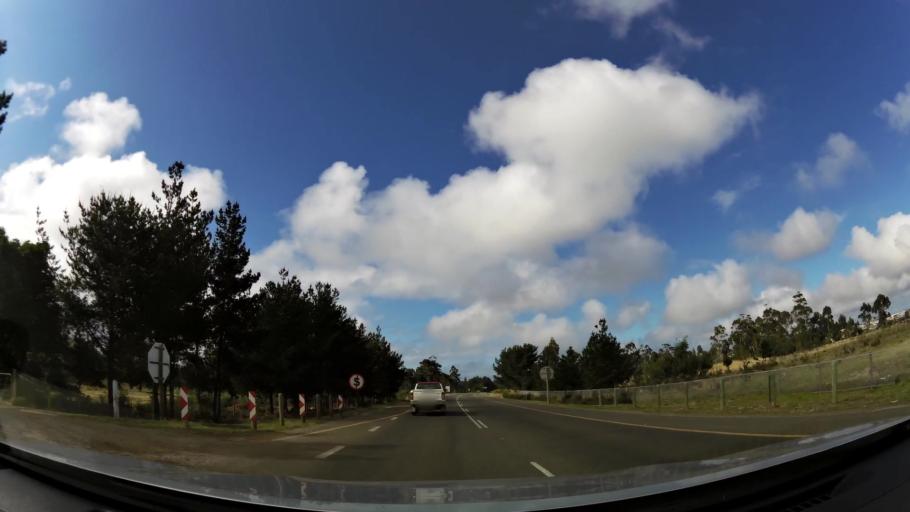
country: ZA
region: Western Cape
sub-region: Eden District Municipality
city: Plettenberg Bay
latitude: -34.0443
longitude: 23.3135
